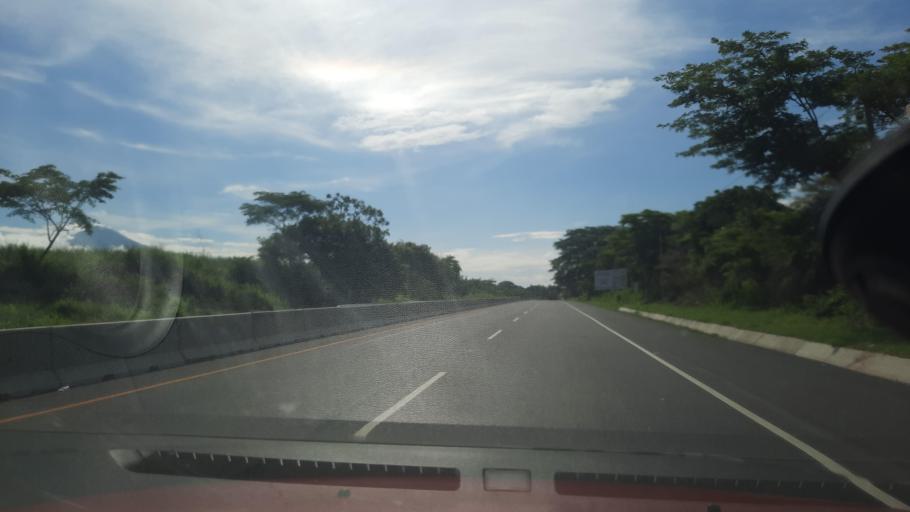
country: SV
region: La Paz
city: Santiago Nonualco
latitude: 13.4853
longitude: -88.9819
